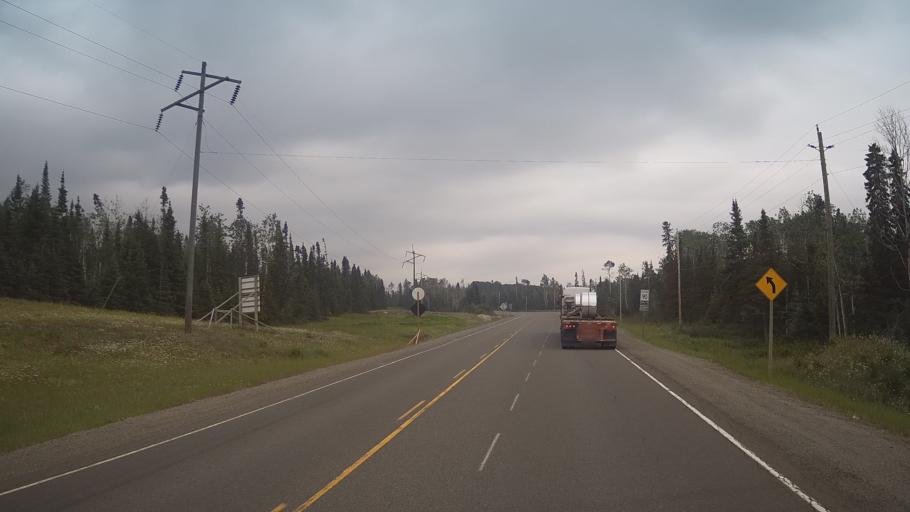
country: CA
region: Ontario
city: Greenstone
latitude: 49.5810
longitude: -87.9725
